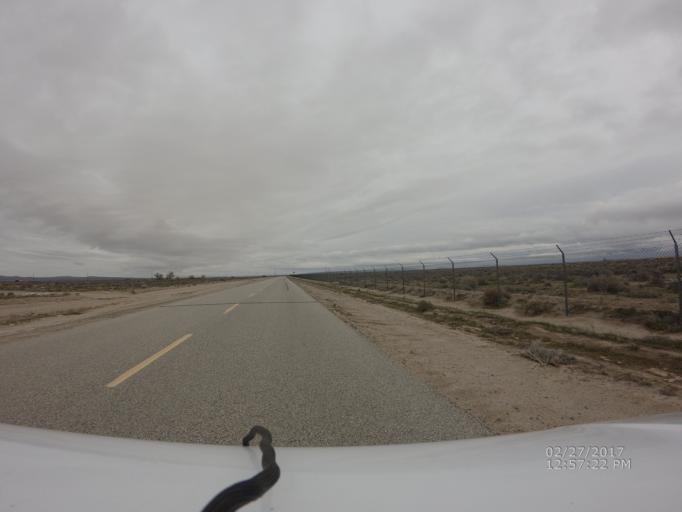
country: US
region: California
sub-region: Kern County
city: Rosamond
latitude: 34.8062
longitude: -118.1583
